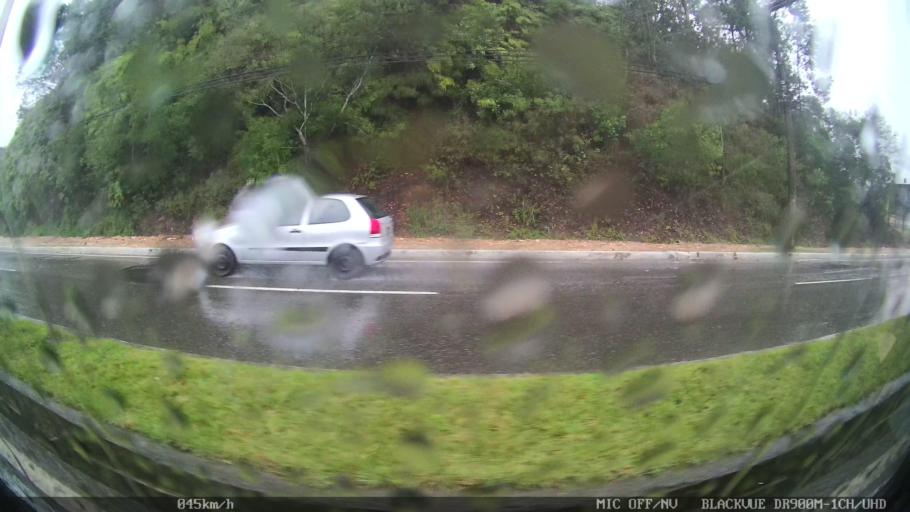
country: BR
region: Santa Catarina
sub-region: Itajai
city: Itajai
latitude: -26.9332
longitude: -48.6425
